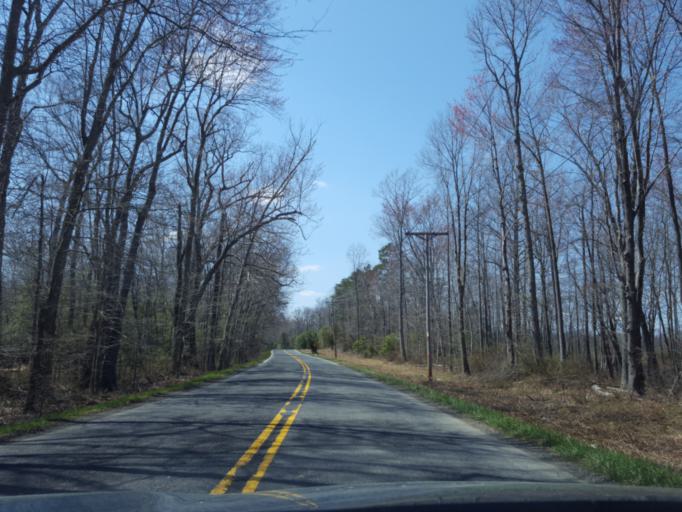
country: US
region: Maryland
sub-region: Prince George's County
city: Brandywine
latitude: 38.6601
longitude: -76.8368
